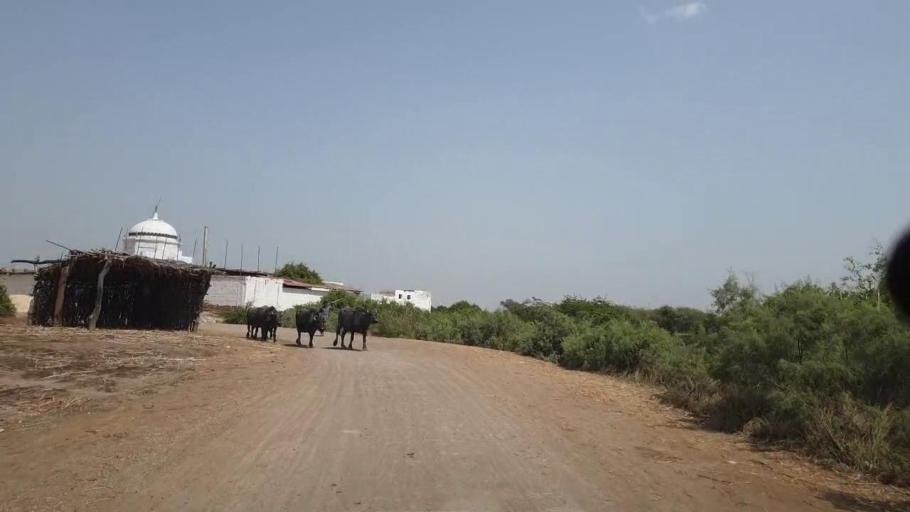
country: PK
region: Sindh
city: Matli
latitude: 25.0718
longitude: 68.7073
